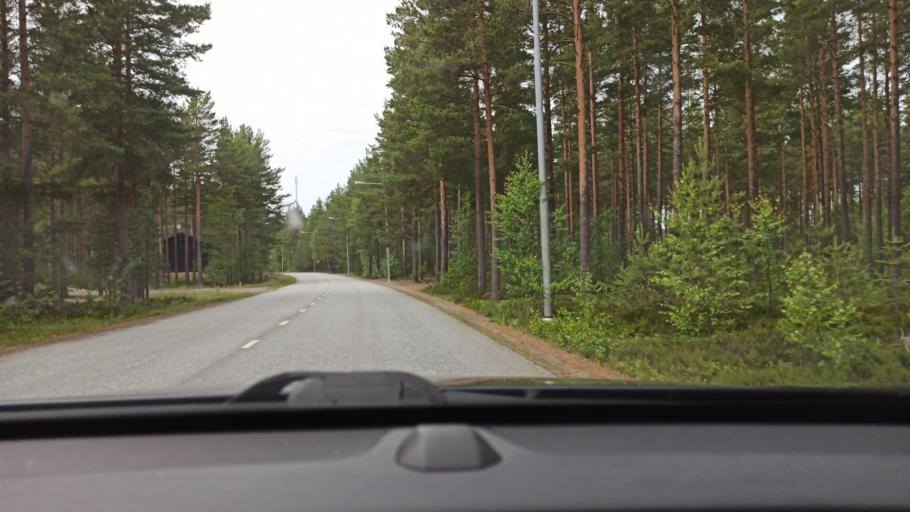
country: FI
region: Satakunta
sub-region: Pori
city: Luvia
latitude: 61.5737
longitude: 21.5289
